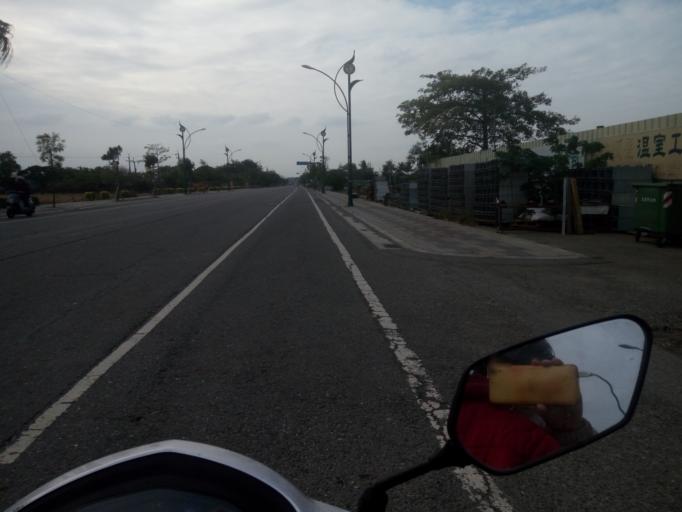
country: TW
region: Taiwan
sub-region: Chiayi
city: Taibao
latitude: 23.4919
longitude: 120.3441
